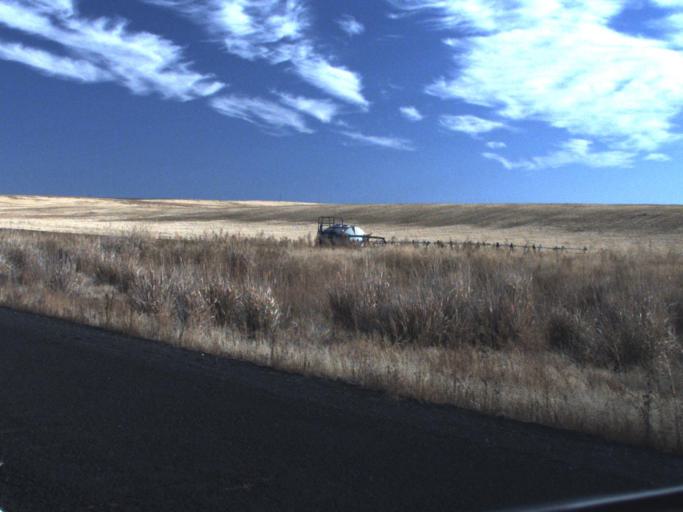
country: US
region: Washington
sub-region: Adams County
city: Ritzville
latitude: 47.0663
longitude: -118.4100
